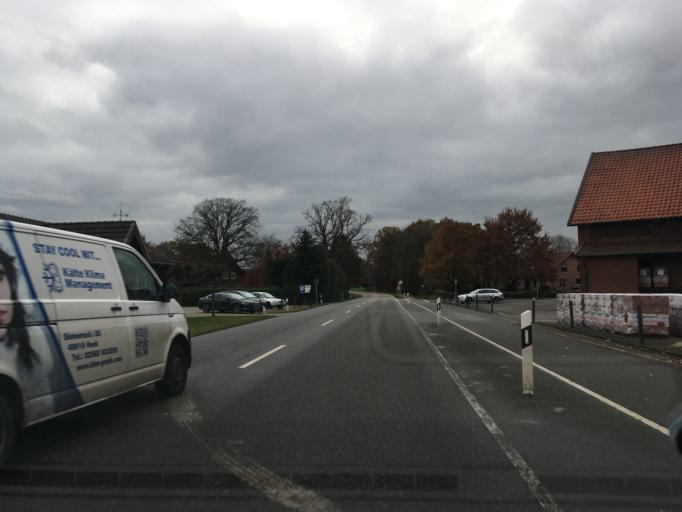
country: DE
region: North Rhine-Westphalia
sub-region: Regierungsbezirk Munster
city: Gescher
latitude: 51.9709
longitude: 7.0142
